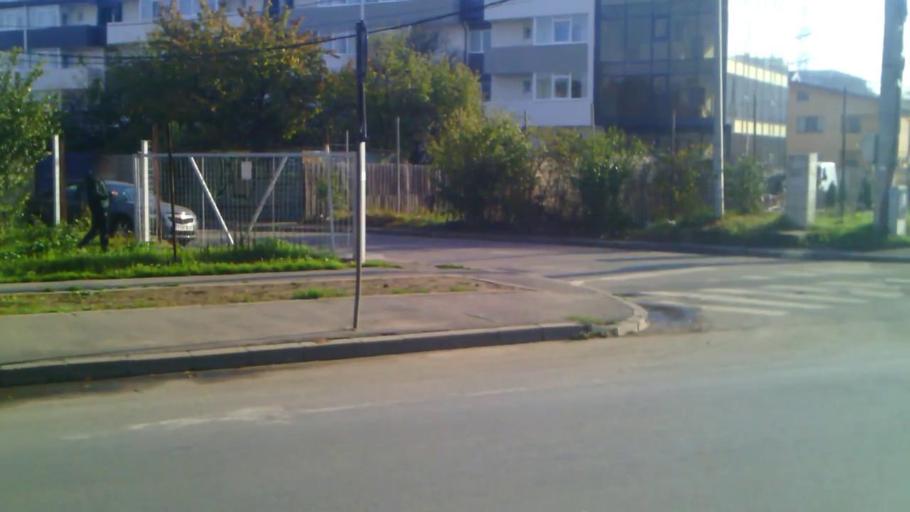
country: RO
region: Ilfov
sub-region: Comuna Popesti-Leordeni
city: Popesti-Leordeni
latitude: 44.3700
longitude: 26.1423
